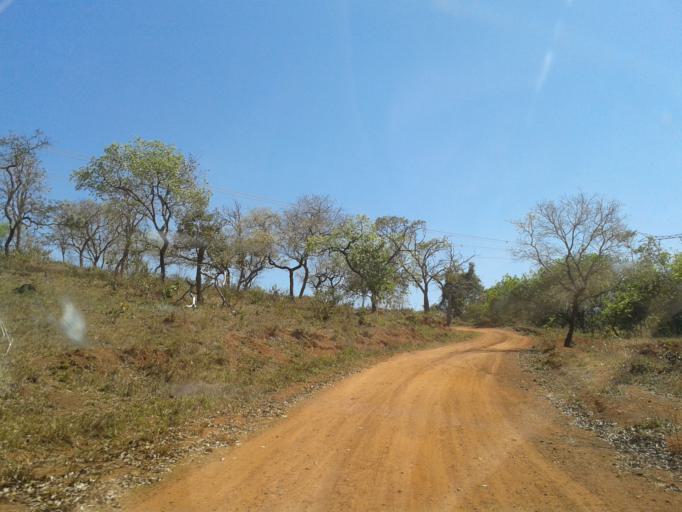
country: BR
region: Minas Gerais
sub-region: Monte Alegre De Minas
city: Monte Alegre de Minas
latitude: -18.8275
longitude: -49.1211
